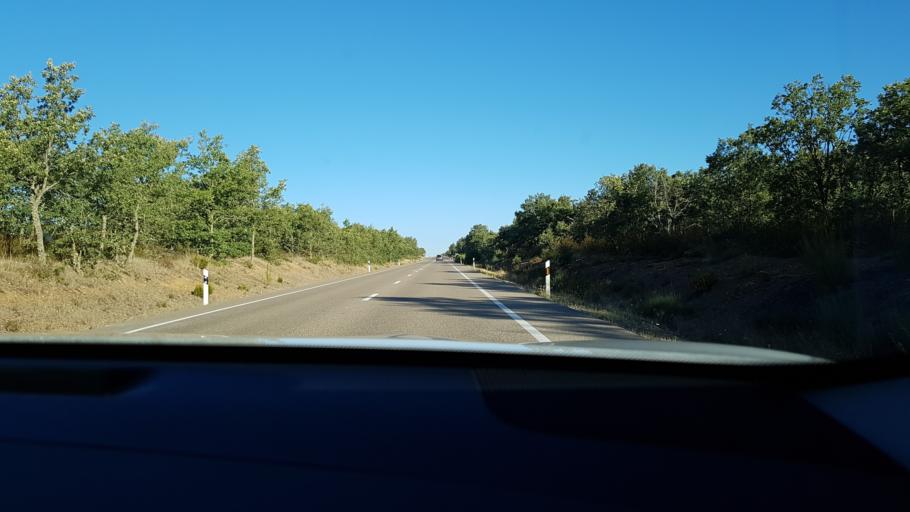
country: ES
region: Castille and Leon
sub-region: Provincia de Zamora
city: Samir de los Canos
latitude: 41.6731
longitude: -6.2361
